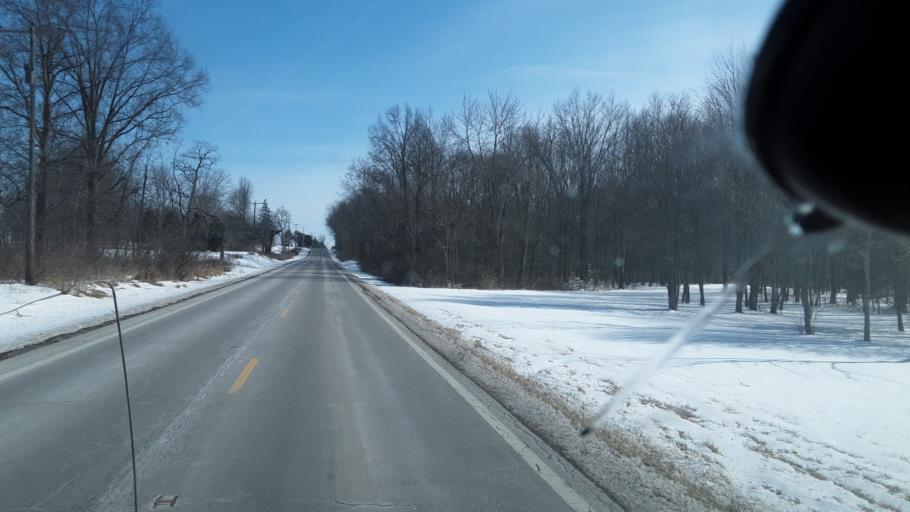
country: US
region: Ohio
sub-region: Mahoning County
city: Sebring
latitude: 40.9562
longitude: -80.9631
